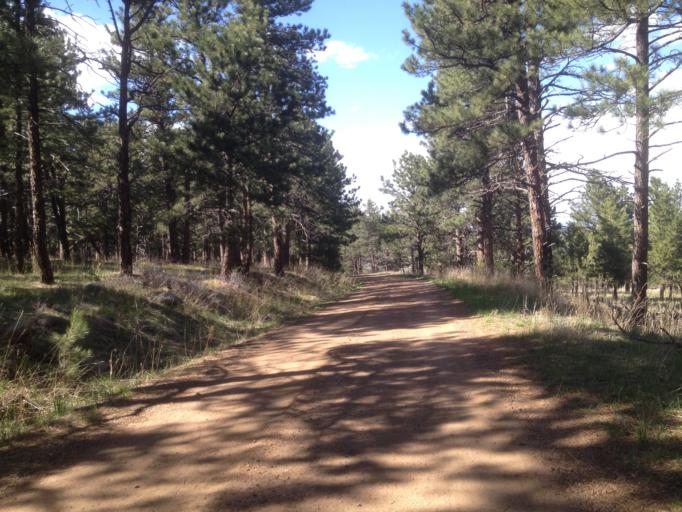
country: US
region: Colorado
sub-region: Boulder County
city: Boulder
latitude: 39.9216
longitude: -105.2712
